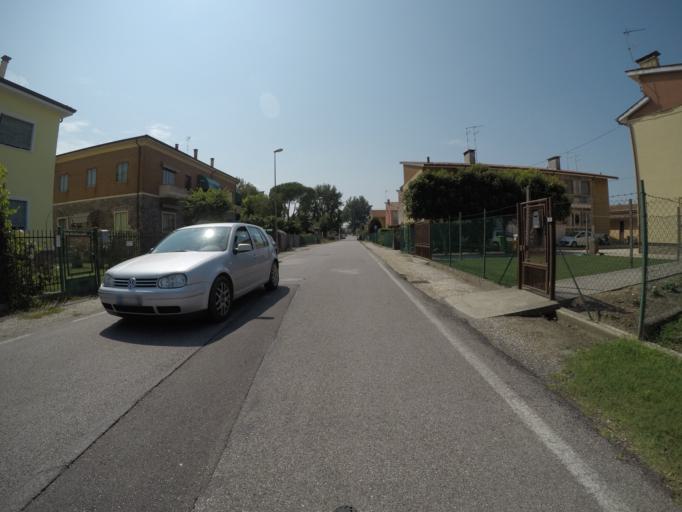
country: IT
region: Veneto
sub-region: Provincia di Rovigo
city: Lendinara
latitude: 45.0882
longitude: 11.5898
